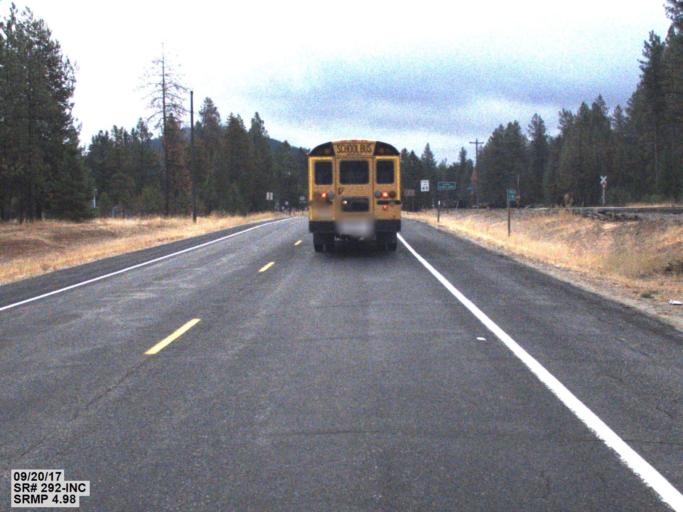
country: US
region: Washington
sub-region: Spokane County
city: Deer Park
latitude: 48.0634
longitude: -117.6389
